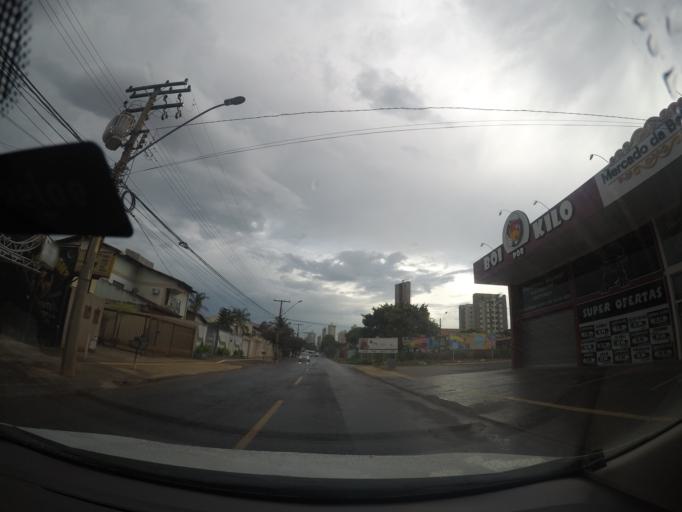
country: BR
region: Goias
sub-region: Goiania
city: Goiania
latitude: -16.7125
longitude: -49.2813
